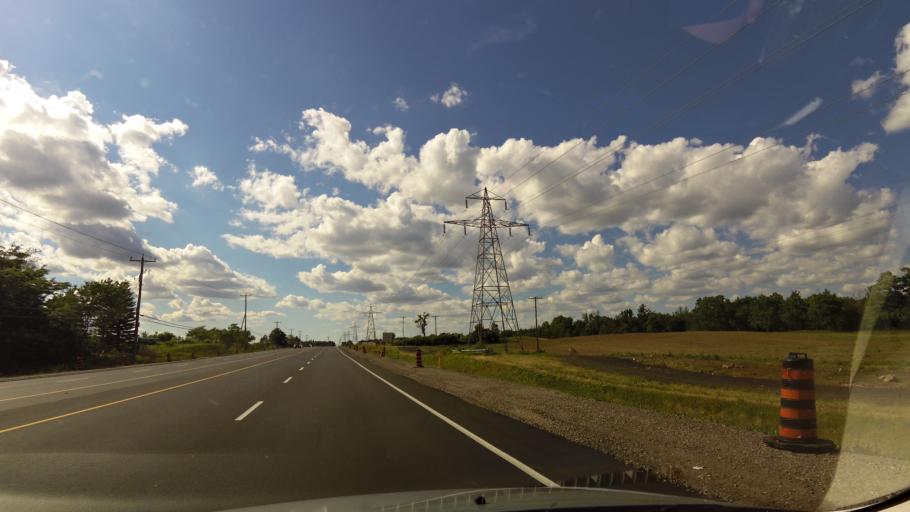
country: CA
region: Ontario
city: Ancaster
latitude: 43.3896
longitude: -80.0228
